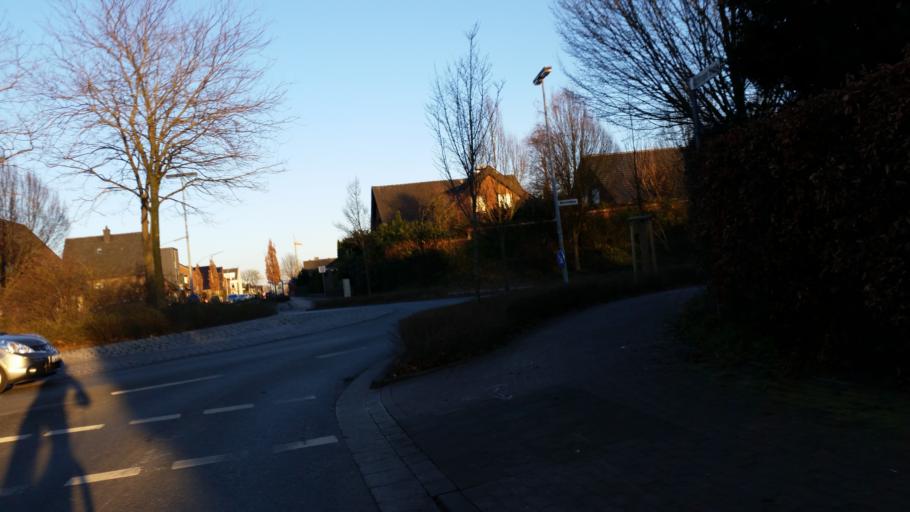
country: DE
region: North Rhine-Westphalia
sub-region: Regierungsbezirk Munster
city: Rheine
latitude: 52.2817
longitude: 7.4109
